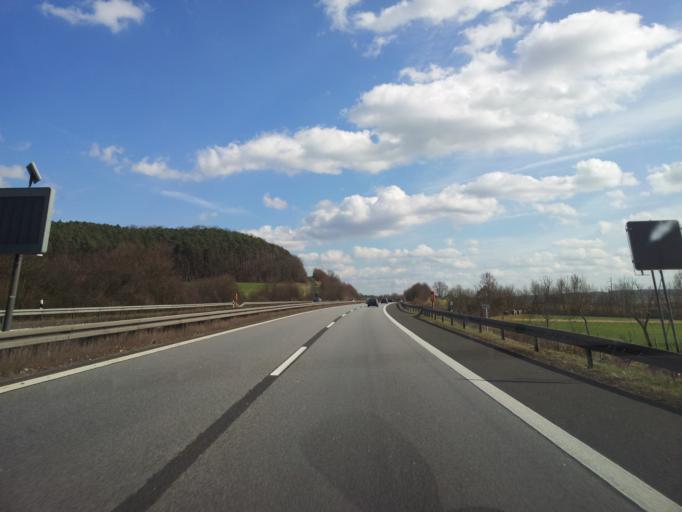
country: DE
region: Bavaria
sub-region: Regierungsbezirk Unterfranken
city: Stettfeld
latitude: 49.9563
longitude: 10.7455
